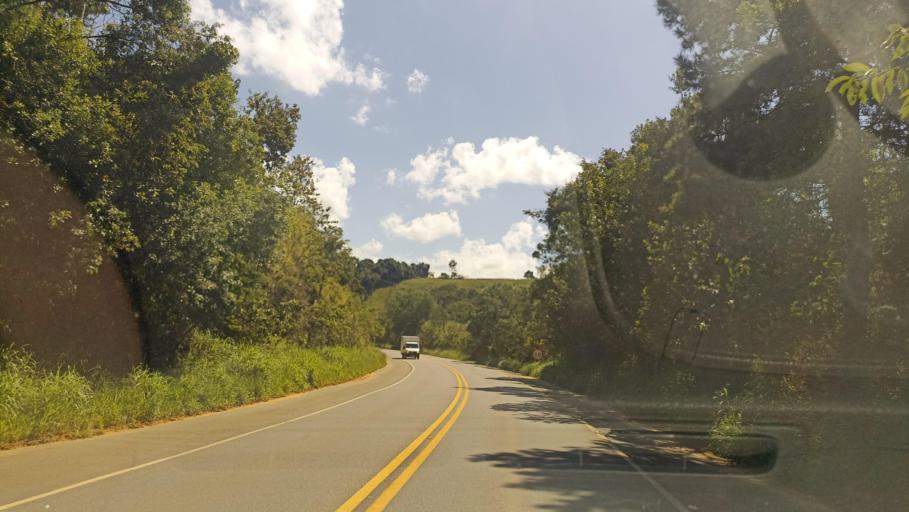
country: BR
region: Sao Paulo
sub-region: Cunha
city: Cunha
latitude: -23.0456
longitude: -45.0048
